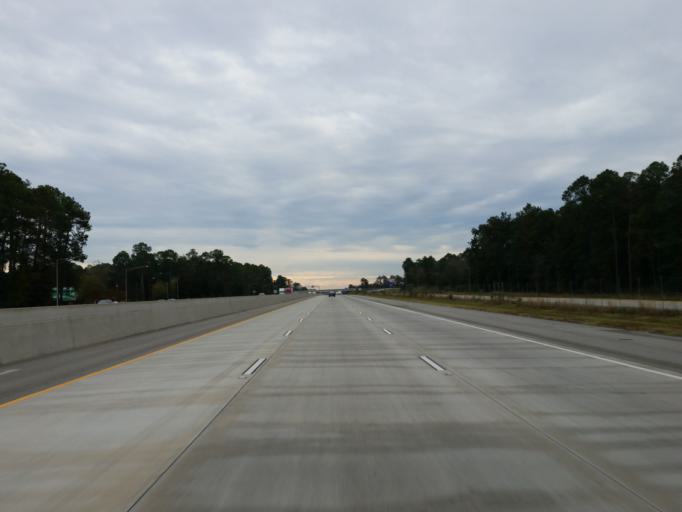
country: US
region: Georgia
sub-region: Cook County
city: Sparks
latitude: 31.2459
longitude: -83.4670
